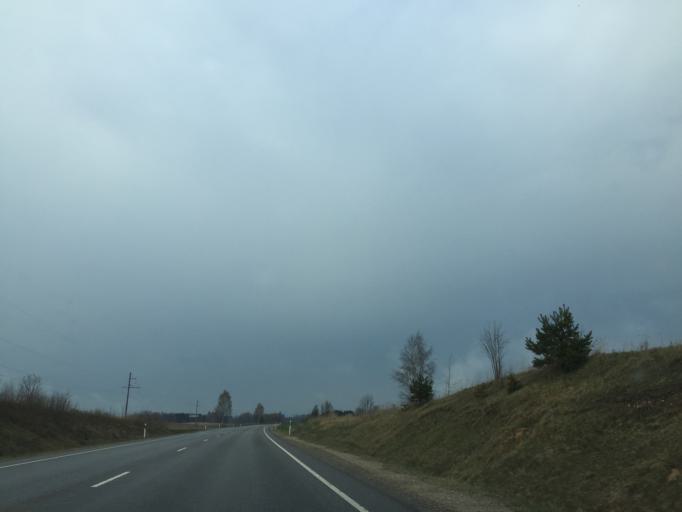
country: EE
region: Tartu
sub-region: UElenurme vald
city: Ulenurme
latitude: 58.1540
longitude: 26.6943
